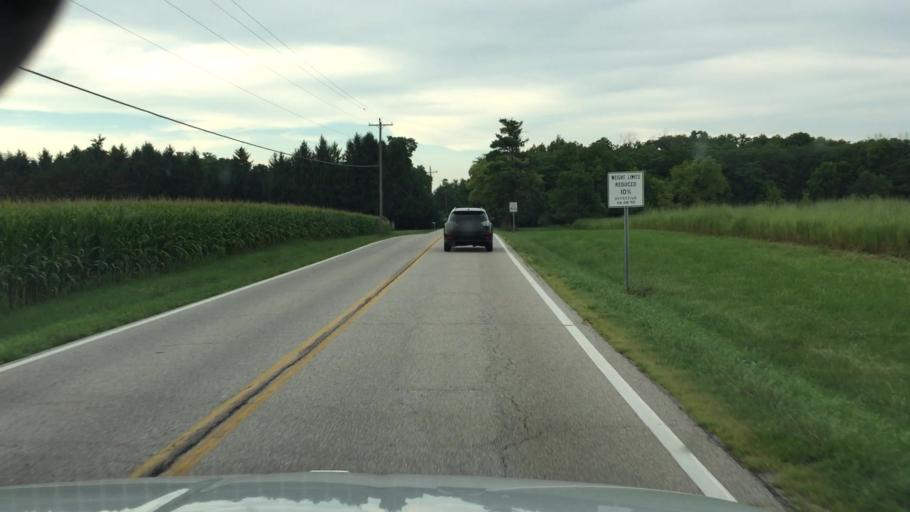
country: US
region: Ohio
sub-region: Madison County
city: West Jefferson
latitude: 39.9985
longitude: -83.2640
